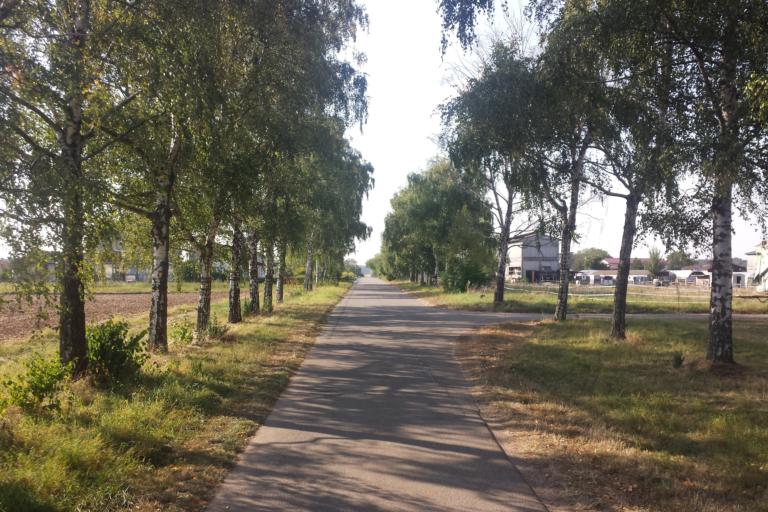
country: DE
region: Baden-Wuerttemberg
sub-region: Karlsruhe Region
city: Plankstadt
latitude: 49.4062
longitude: 8.5874
